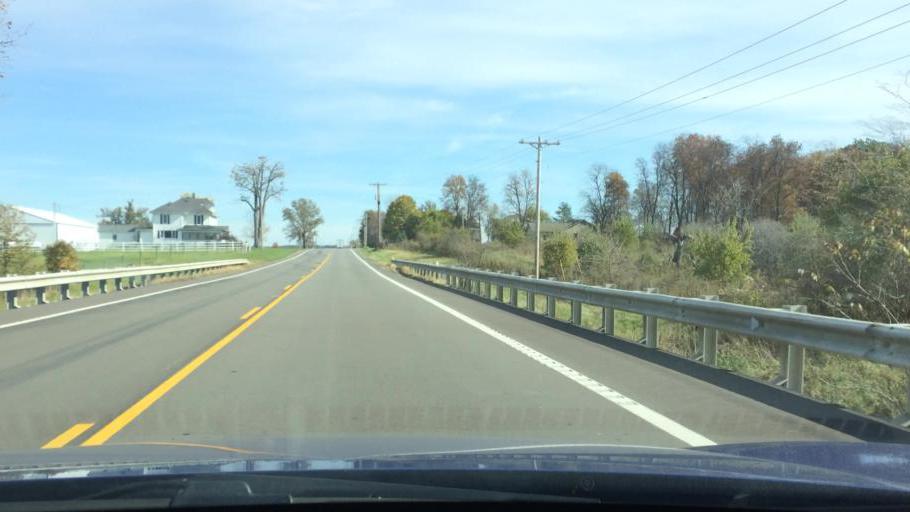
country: US
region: Ohio
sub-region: Logan County
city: Russells Point
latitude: 40.4444
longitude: -83.8344
